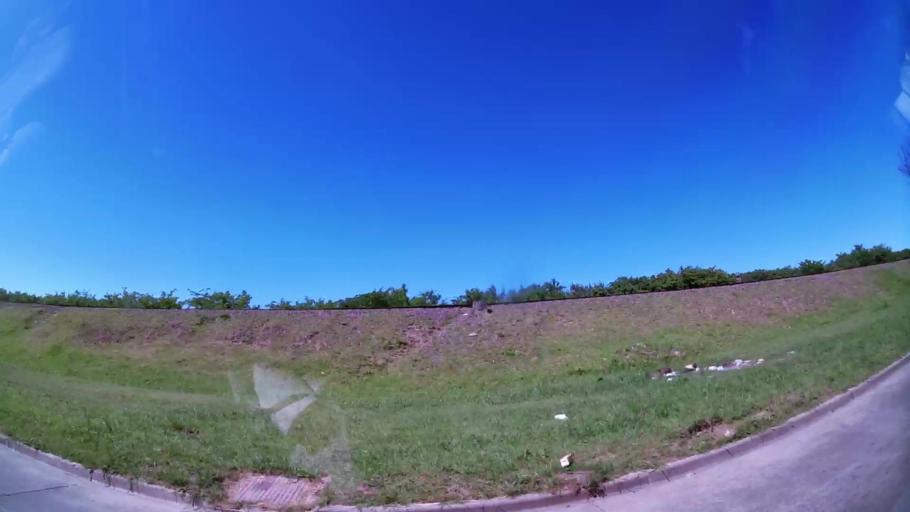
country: AR
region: Buenos Aires
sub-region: Partido de Tigre
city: Tigre
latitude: -34.5042
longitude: -58.6141
